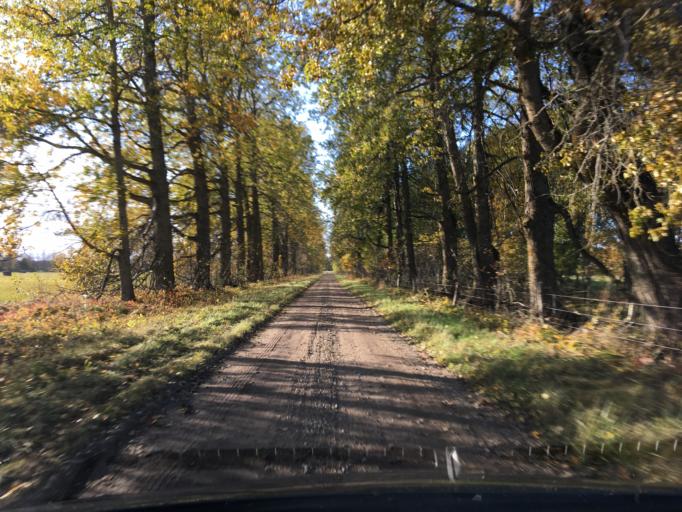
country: EE
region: Laeaene
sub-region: Lihula vald
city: Lihula
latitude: 58.5643
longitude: 23.7946
